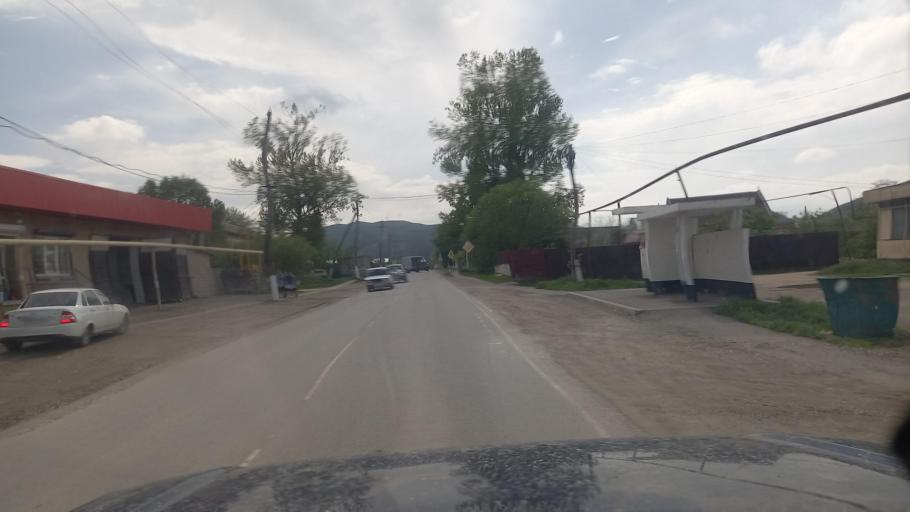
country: RU
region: Kabardino-Balkariya
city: Sarmakovo
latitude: 43.7365
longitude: 43.1796
